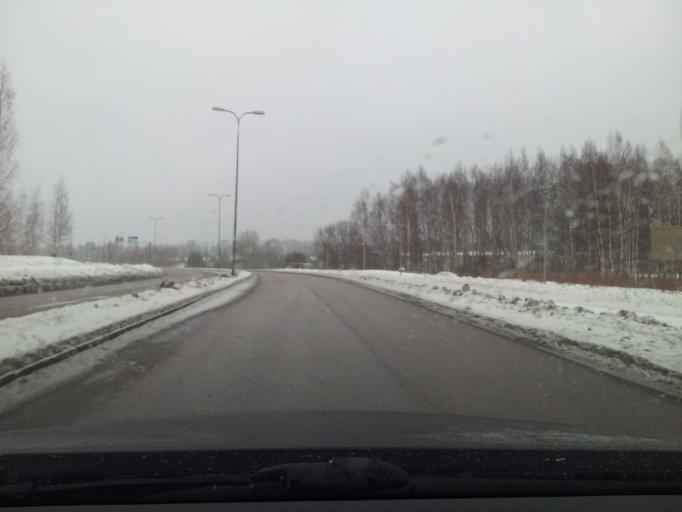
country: FI
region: Uusimaa
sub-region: Helsinki
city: Koukkuniemi
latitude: 60.1801
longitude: 24.7792
